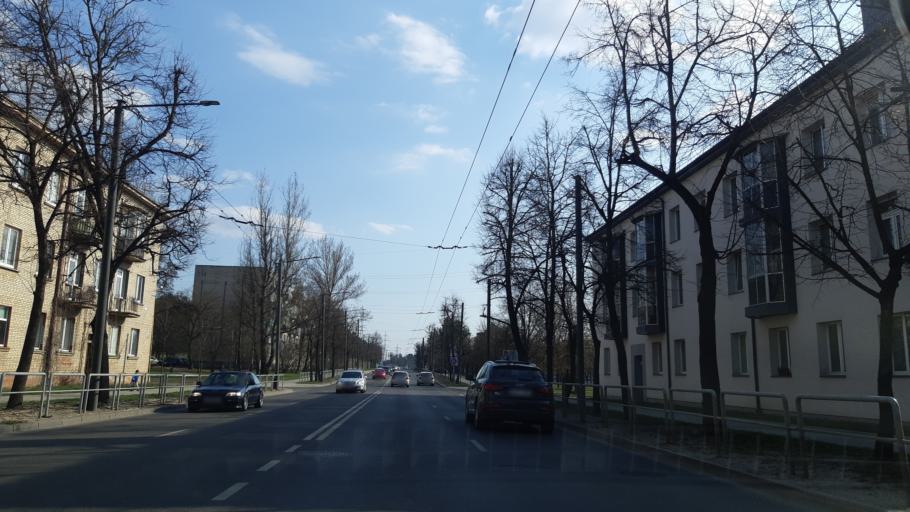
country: LT
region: Kauno apskritis
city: Dainava (Kaunas)
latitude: 54.8894
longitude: 24.0048
